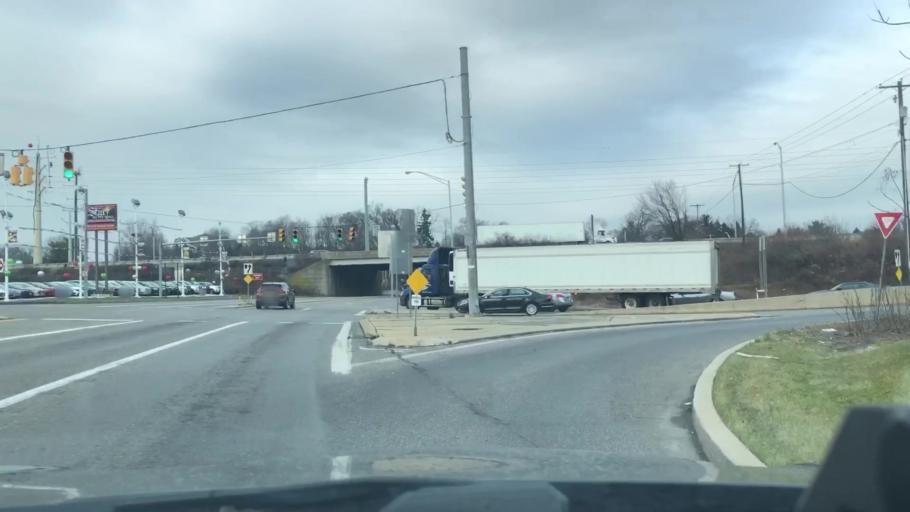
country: US
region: Pennsylvania
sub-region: Northampton County
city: Bethlehem
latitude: 40.6620
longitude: -75.3828
